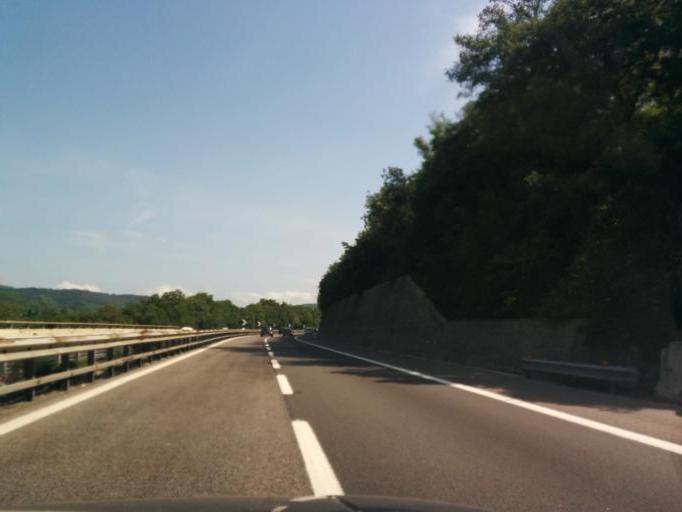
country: IT
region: Tuscany
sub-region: Province of Florence
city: Carraia
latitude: 43.9158
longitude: 11.1974
